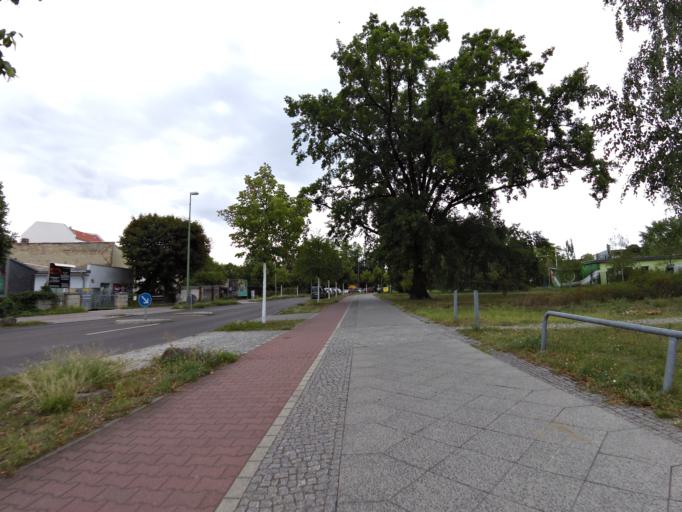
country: DE
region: Berlin
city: Johannisthal
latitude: 52.4412
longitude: 13.5078
